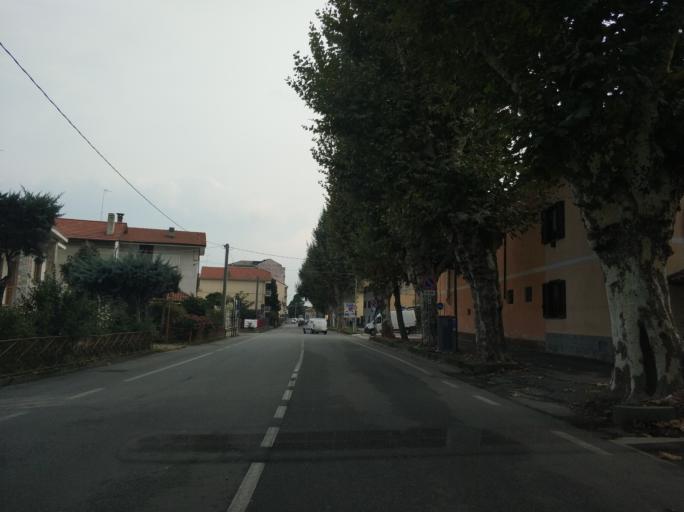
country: IT
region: Piedmont
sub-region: Provincia di Torino
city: San Carlo Canavese
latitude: 45.2392
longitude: 7.6019
